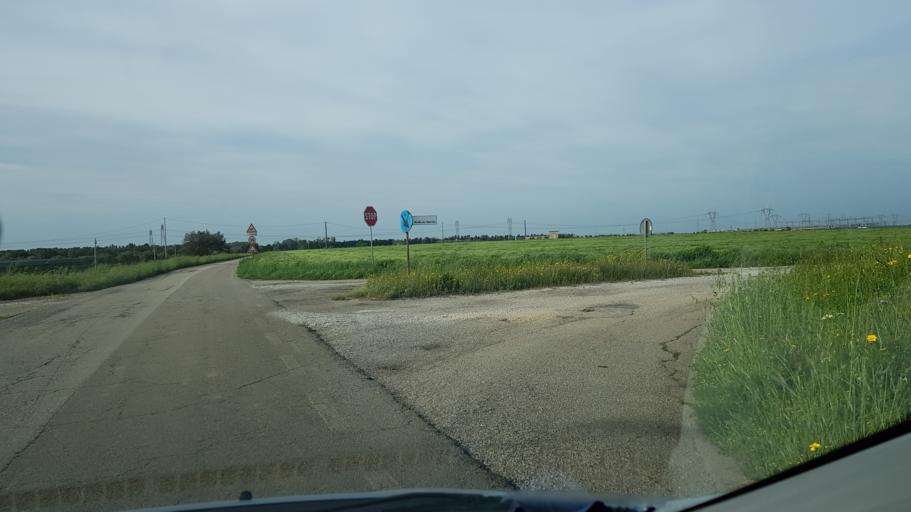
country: IT
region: Apulia
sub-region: Provincia di Brindisi
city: Tuturano
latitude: 40.5341
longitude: 17.8919
